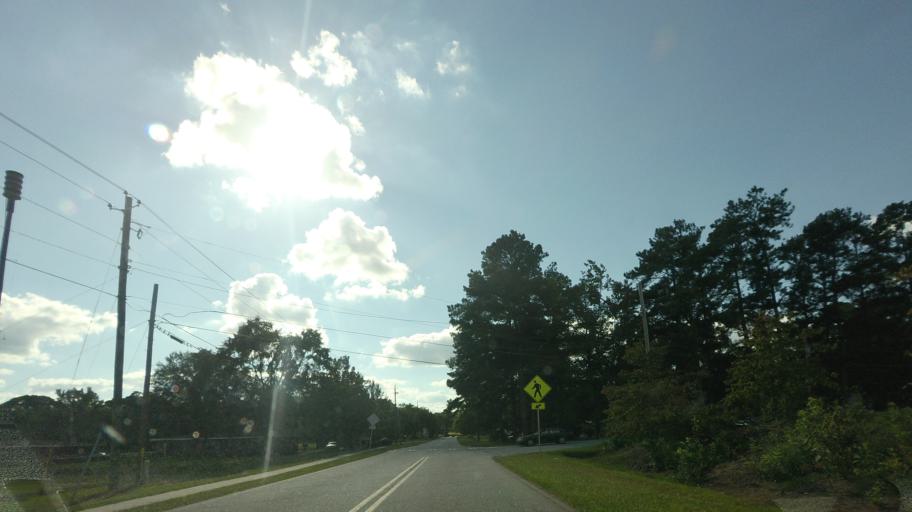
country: US
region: Georgia
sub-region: Lamar County
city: Barnesville
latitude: 33.0441
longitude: -84.1417
